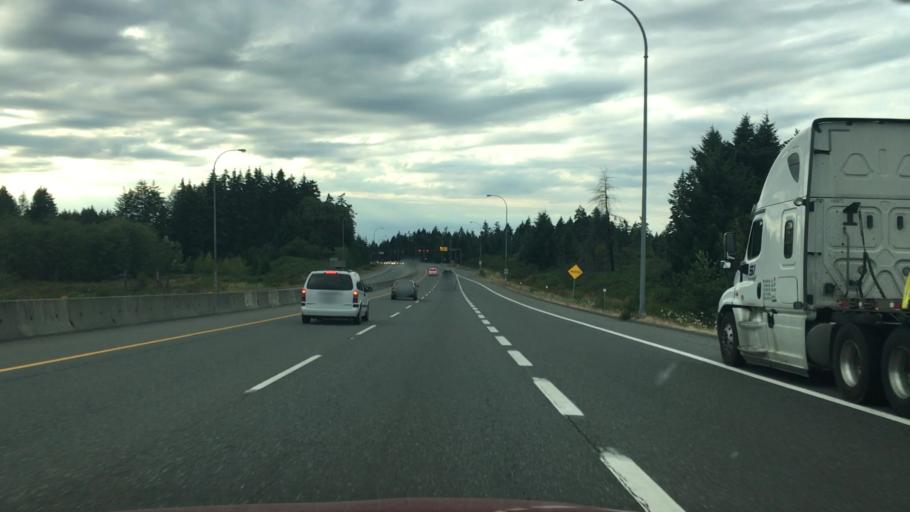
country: CA
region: British Columbia
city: Nanaimo
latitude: 49.2381
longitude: -124.0563
